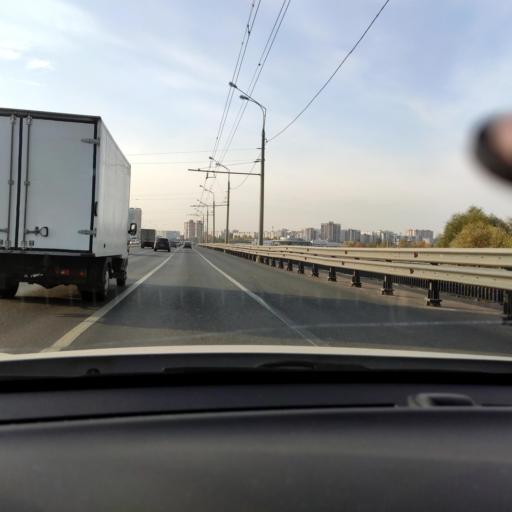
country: RU
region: Tatarstan
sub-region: Gorod Kazan'
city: Kazan
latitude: 55.8204
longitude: 49.1692
